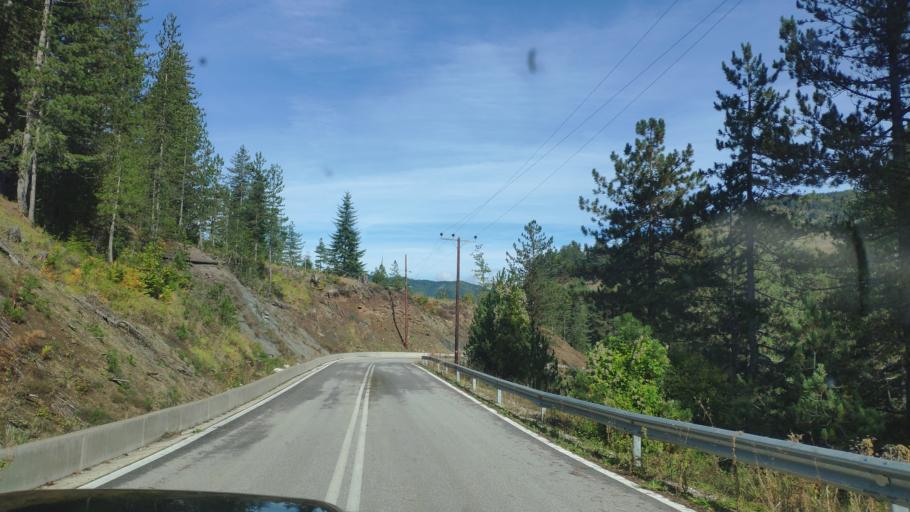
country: AL
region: Korce
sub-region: Rrethi i Devollit
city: Miras
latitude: 40.4079
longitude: 20.8777
